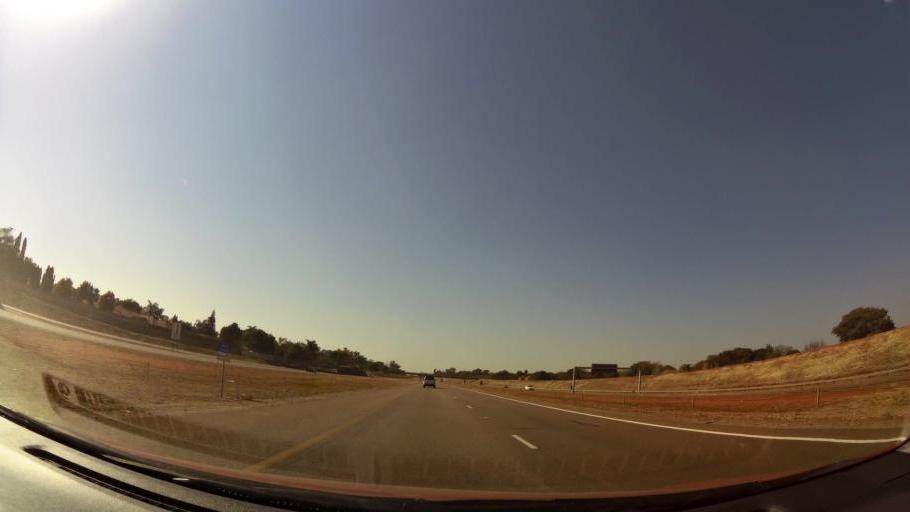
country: ZA
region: Gauteng
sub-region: City of Tshwane Metropolitan Municipality
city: Pretoria
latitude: -25.6541
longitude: 28.1190
